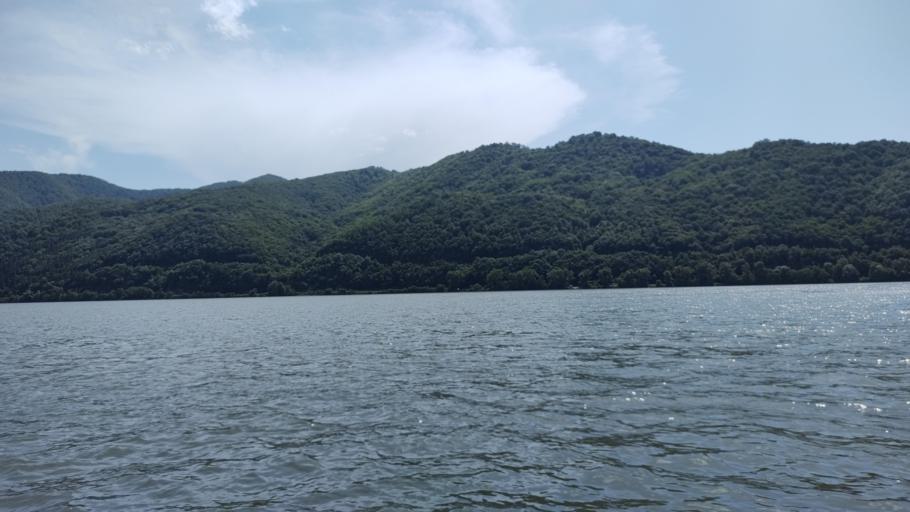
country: RS
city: Radenka
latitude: 44.6560
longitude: 21.8088
